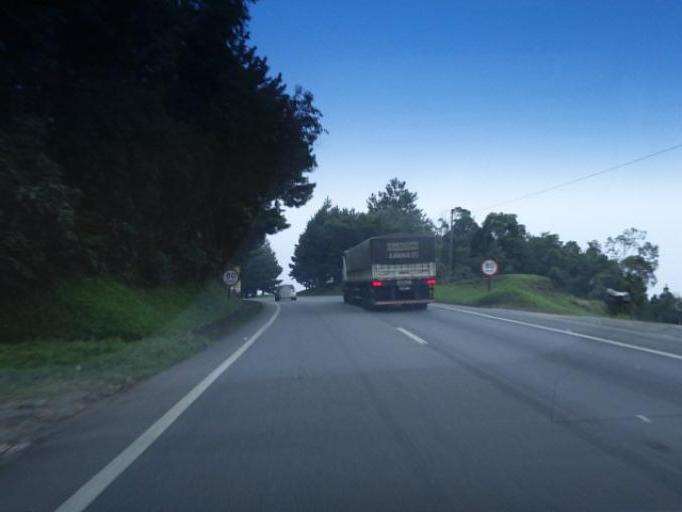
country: BR
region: Parana
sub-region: Sao Jose Dos Pinhais
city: Sao Jose dos Pinhais
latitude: -25.8531
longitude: -49.0292
